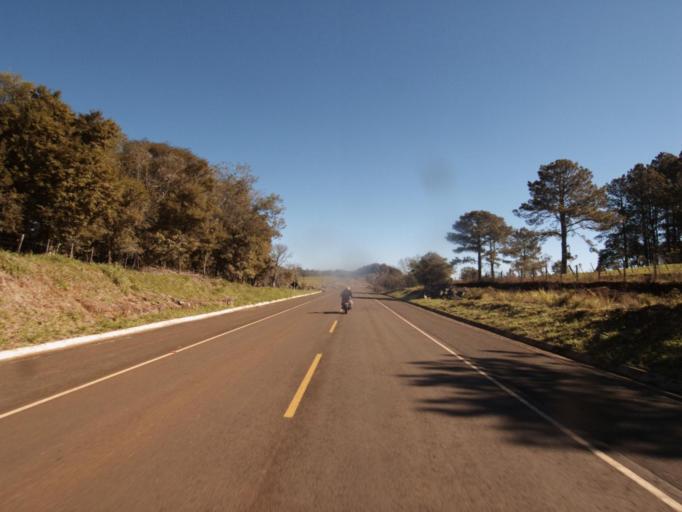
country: AR
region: Misiones
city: Bernardo de Irigoyen
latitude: -26.6136
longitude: -53.7028
